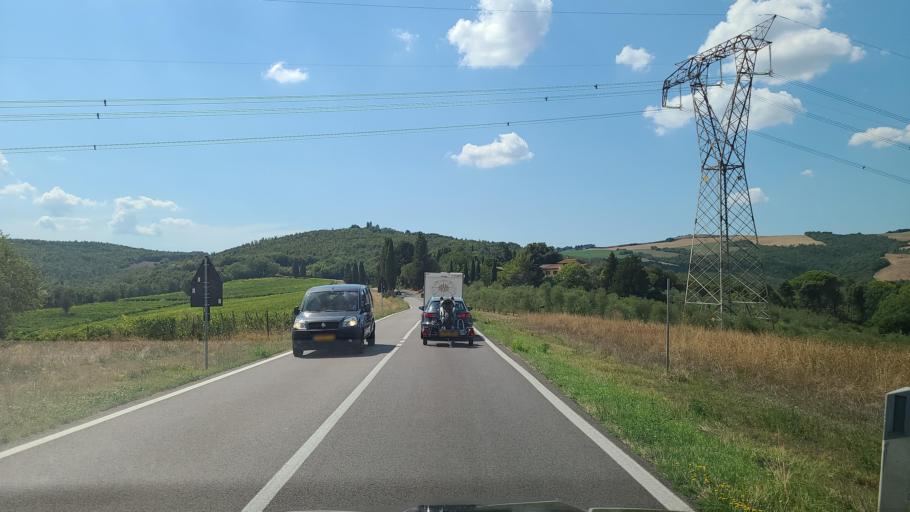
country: IT
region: Tuscany
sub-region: Provincia di Siena
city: San Gimignano
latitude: 43.4043
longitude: 11.0097
